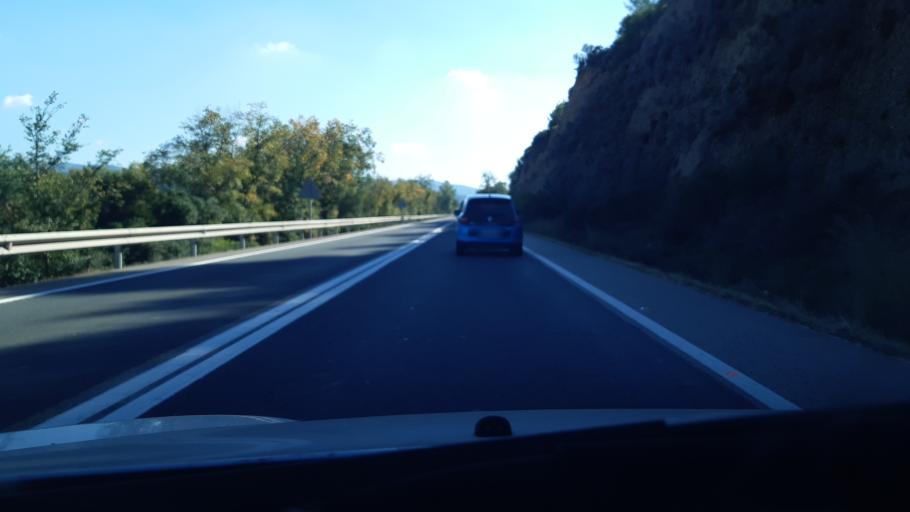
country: ES
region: Catalonia
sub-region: Provincia de Tarragona
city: Tivenys
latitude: 40.8610
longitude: 0.5090
